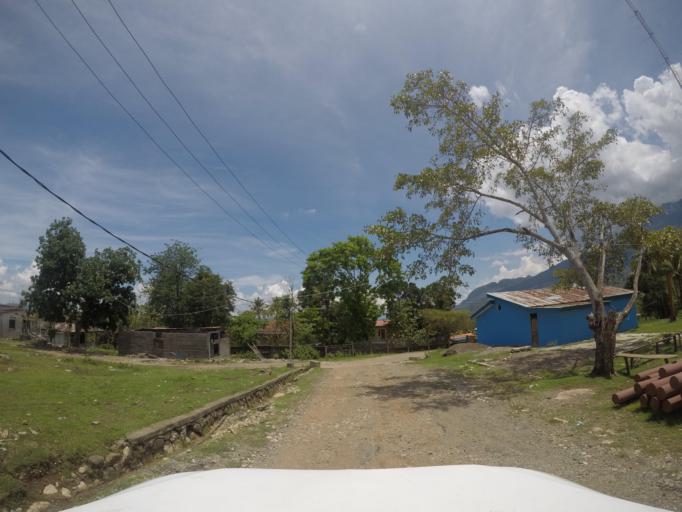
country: TL
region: Bobonaro
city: Maliana
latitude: -8.9955
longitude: 125.2178
